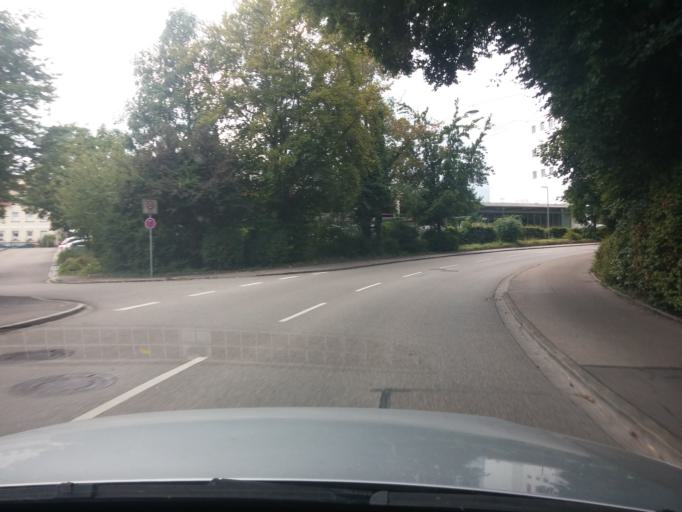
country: DE
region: Bavaria
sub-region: Swabia
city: Memmingen
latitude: 47.9799
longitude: 10.1803
